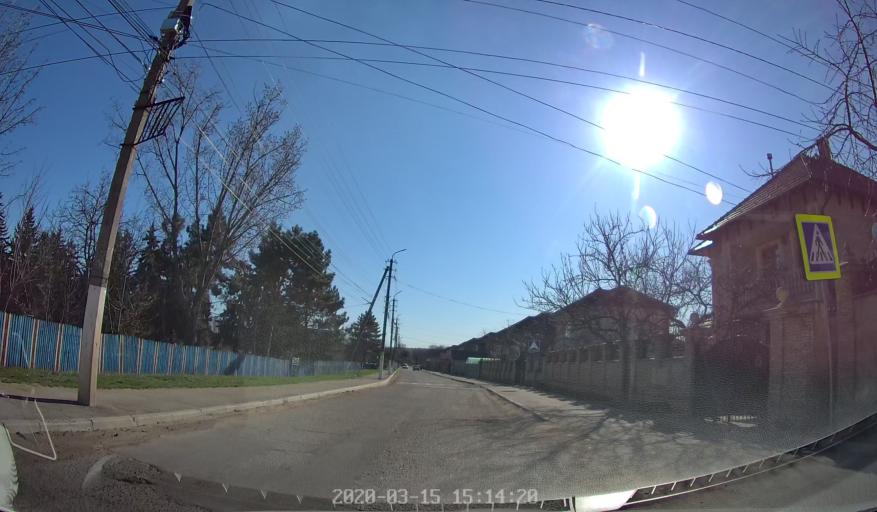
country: MD
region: Chisinau
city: Cricova
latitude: 47.2467
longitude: 28.7670
